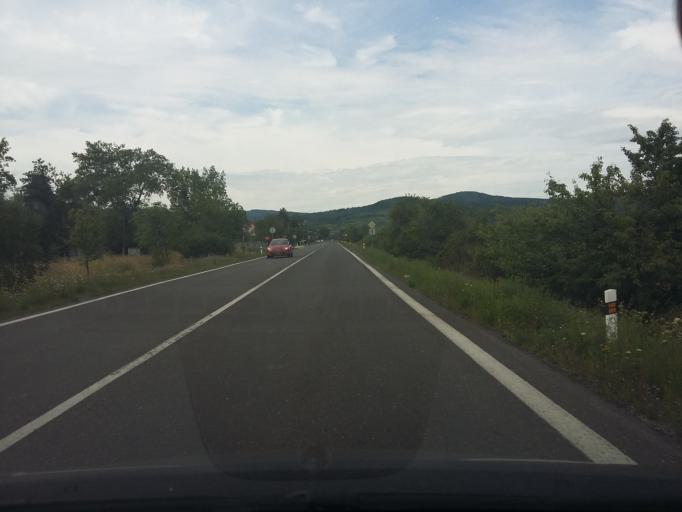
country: SK
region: Bratislavsky
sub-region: Okres Pezinok
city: Pezinok
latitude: 48.3108
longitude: 17.2687
